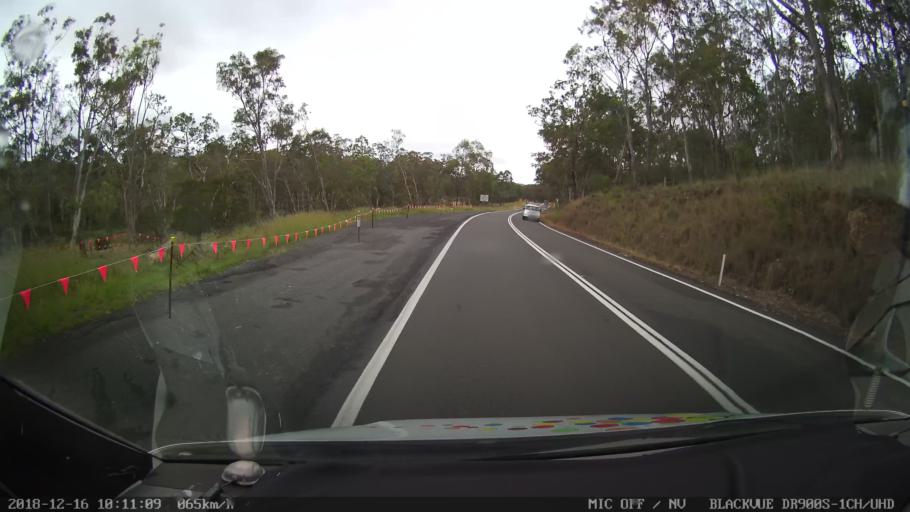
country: AU
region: New South Wales
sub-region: Glen Innes Severn
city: Glen Innes
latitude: -29.3148
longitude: 151.9302
